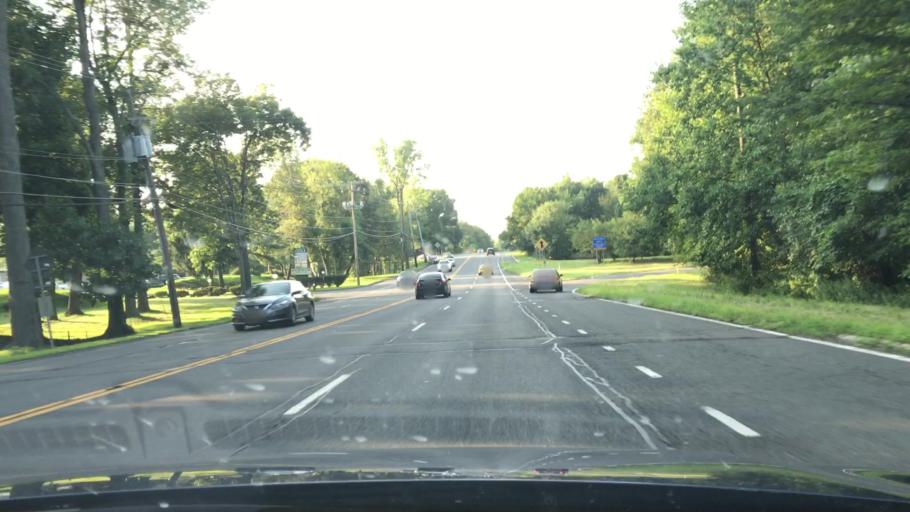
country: US
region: New York
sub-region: Rockland County
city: Tappan
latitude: 41.0330
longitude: -73.9451
